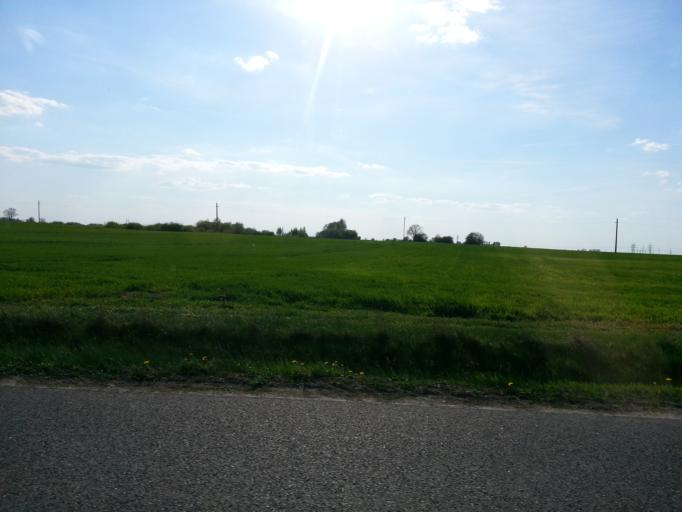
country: LT
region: Panevezys
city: Pasvalys
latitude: 55.9161
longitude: 24.3351
